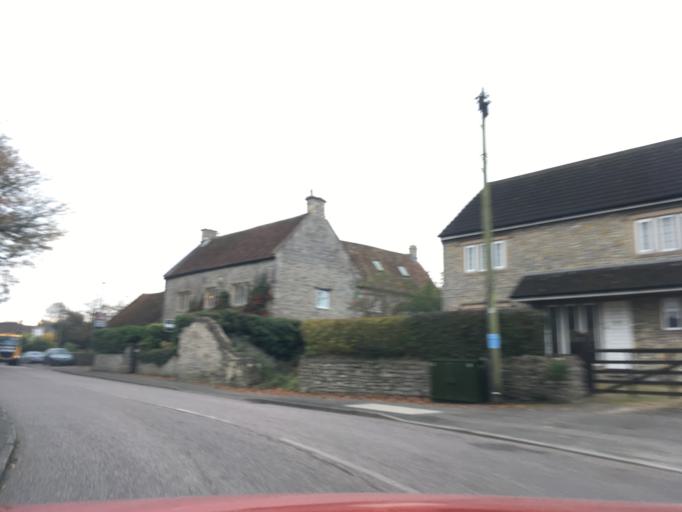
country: GB
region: England
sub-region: South Gloucestershire
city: Pucklechurch
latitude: 51.4871
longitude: -2.4353
